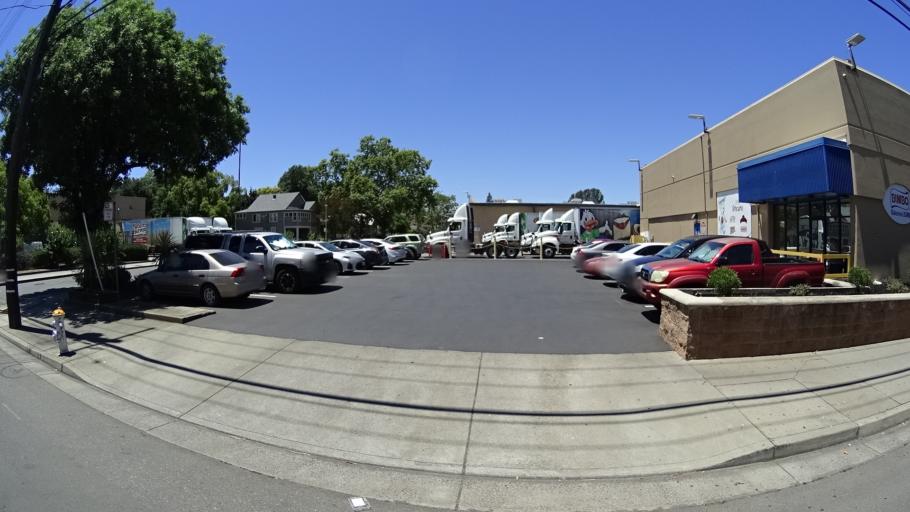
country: US
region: California
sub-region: Sacramento County
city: Sacramento
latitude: 38.5464
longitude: -121.4713
